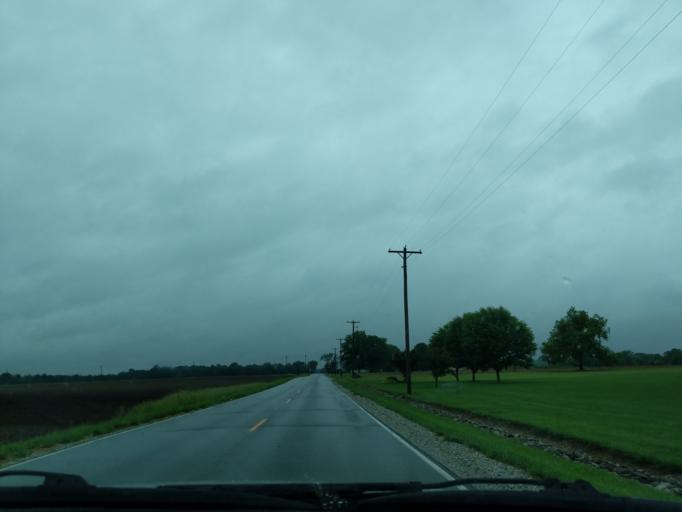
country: US
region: Indiana
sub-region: Madison County
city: Lapel
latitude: 40.0665
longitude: -85.9064
